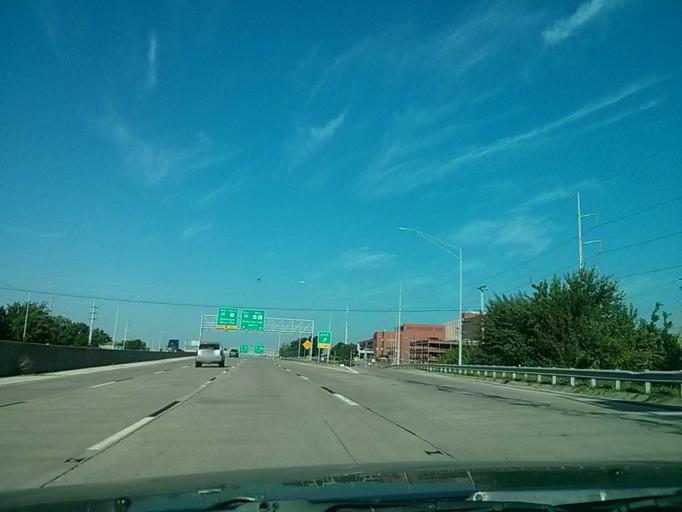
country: US
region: Oklahoma
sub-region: Tulsa County
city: Tulsa
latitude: 36.1454
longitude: -95.9958
